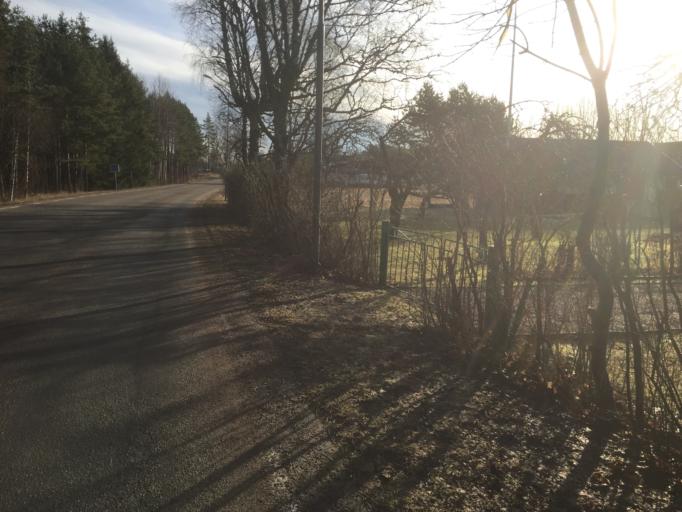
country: SE
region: Joenkoeping
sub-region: Aneby Kommun
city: Aneby
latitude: 57.8467
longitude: 14.7973
